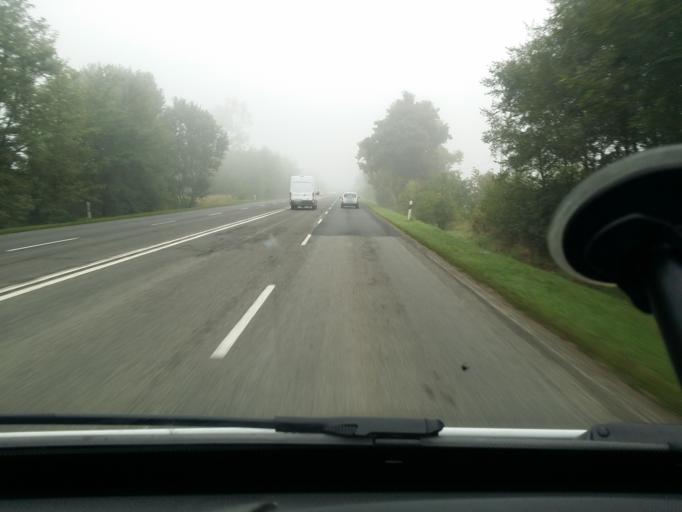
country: HU
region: Bacs-Kiskun
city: Kecskemet
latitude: 46.9531
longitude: 19.6490
